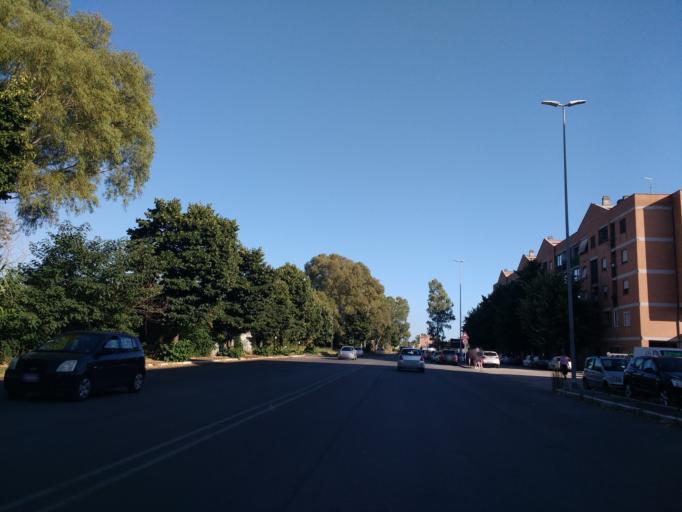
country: IT
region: Latium
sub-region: Citta metropolitana di Roma Capitale
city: Acilia-Castel Fusano-Ostia Antica
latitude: 41.7750
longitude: 12.3529
